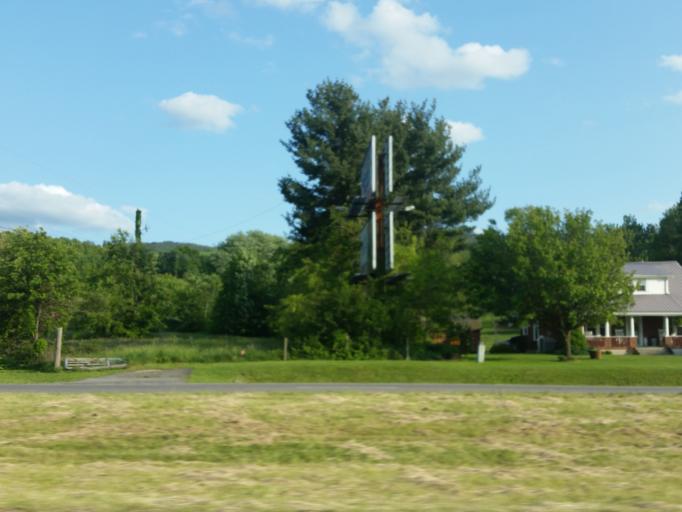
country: US
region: Virginia
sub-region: Russell County
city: Honaker
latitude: 36.9745
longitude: -81.8891
